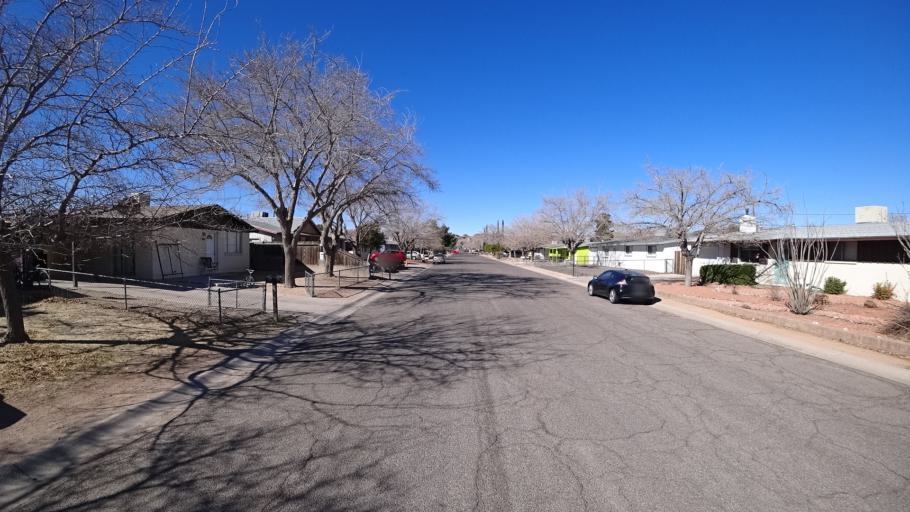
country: US
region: Arizona
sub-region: Mohave County
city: Kingman
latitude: 35.2112
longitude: -114.0323
